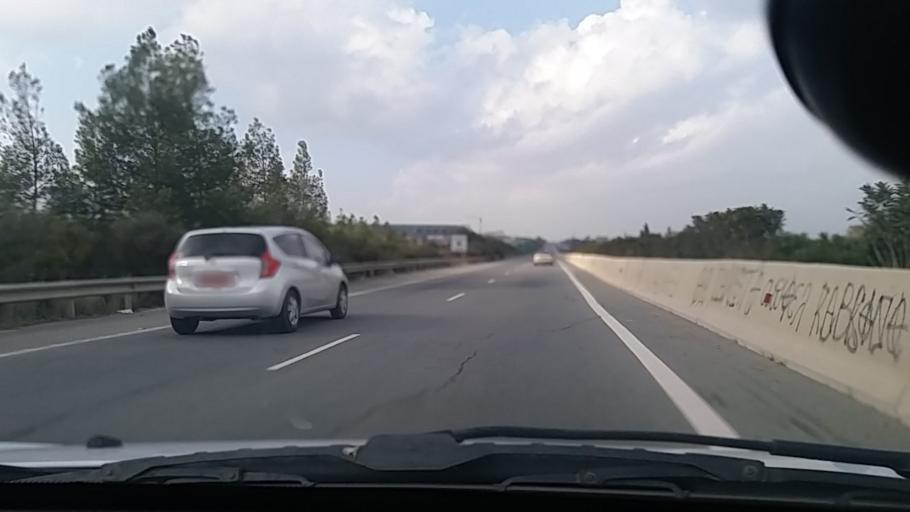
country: CY
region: Lefkosia
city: Kato Deftera
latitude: 35.1314
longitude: 33.2888
